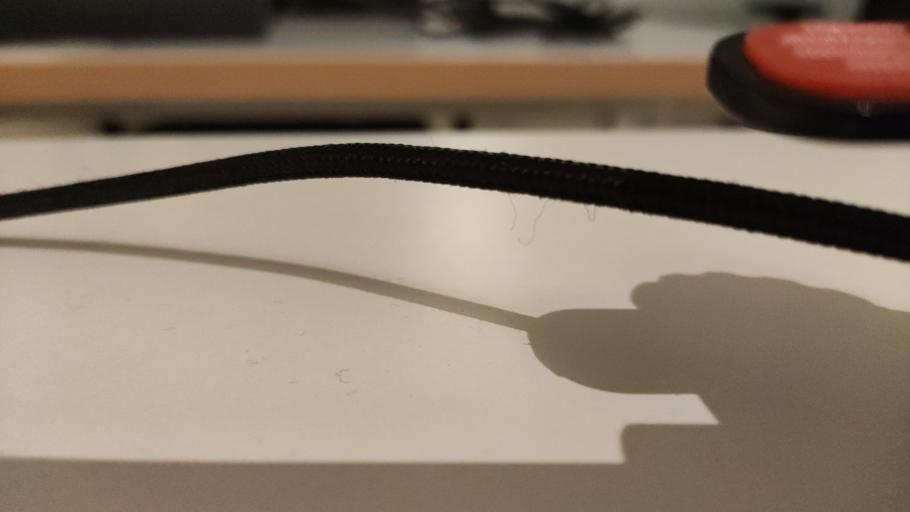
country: RU
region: Moskovskaya
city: Bogorodskoye
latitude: 56.4406
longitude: 37.9036
